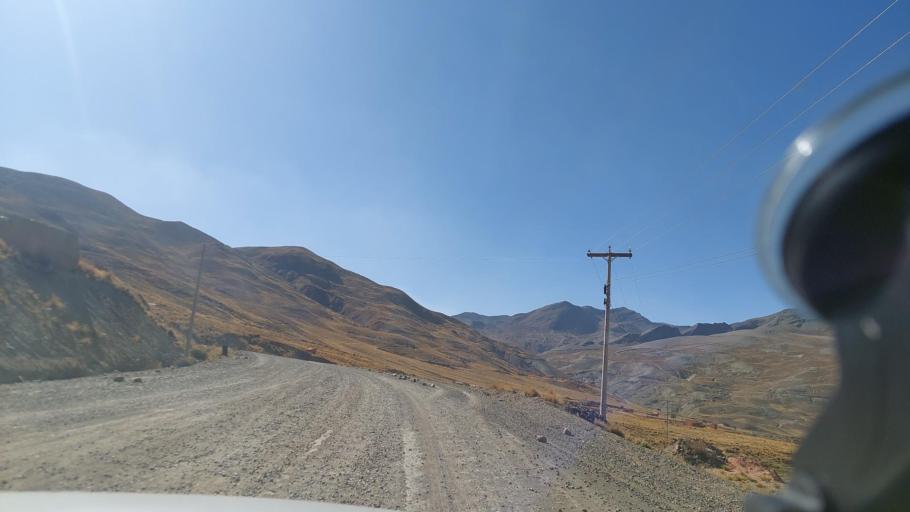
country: BO
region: La Paz
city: La Paz
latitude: -16.4006
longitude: -68.1033
